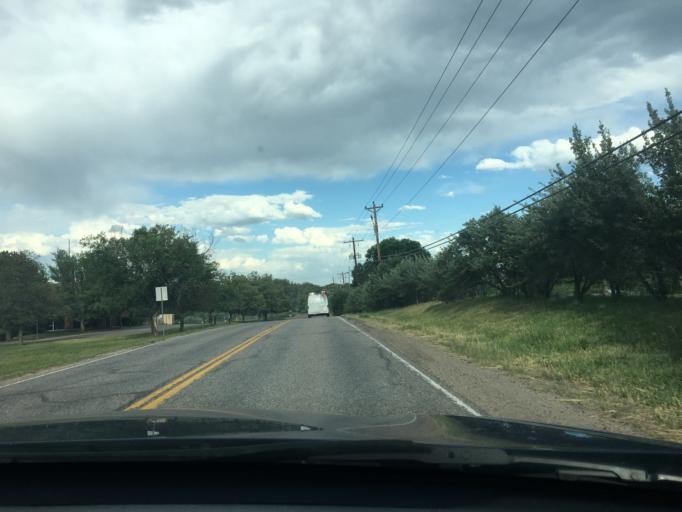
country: US
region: Colorado
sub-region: Jefferson County
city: Applewood
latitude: 39.7614
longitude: -105.1772
